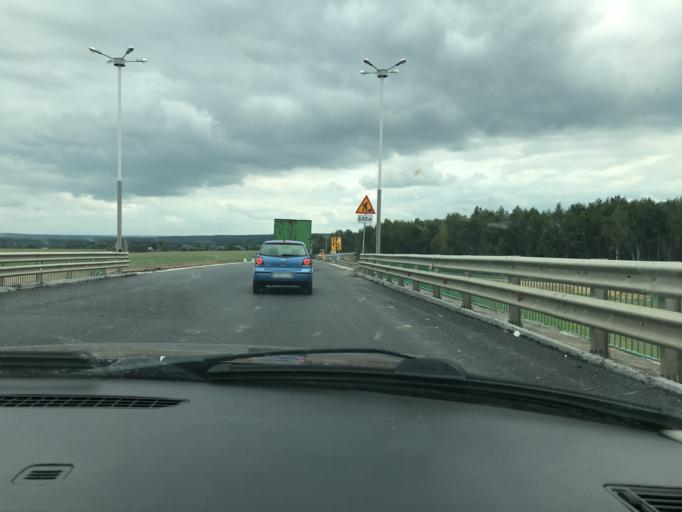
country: RU
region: Kaluga
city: Detchino
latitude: 54.7745
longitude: 36.2385
